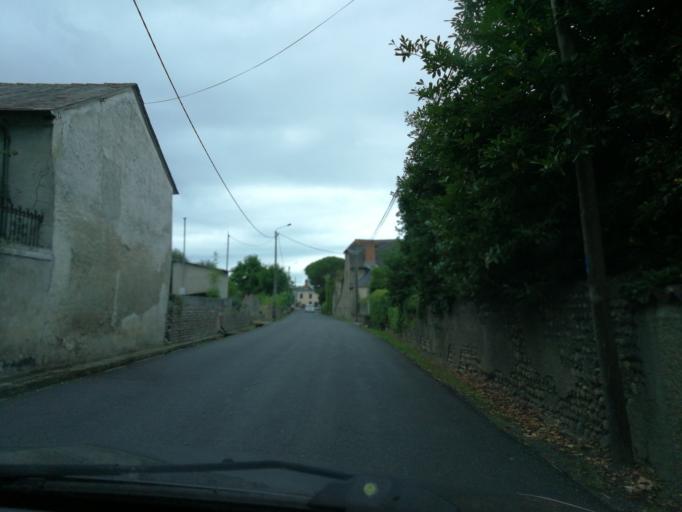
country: FR
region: Midi-Pyrenees
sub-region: Departement des Hautes-Pyrenees
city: Bazet
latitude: 43.2771
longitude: 0.0914
